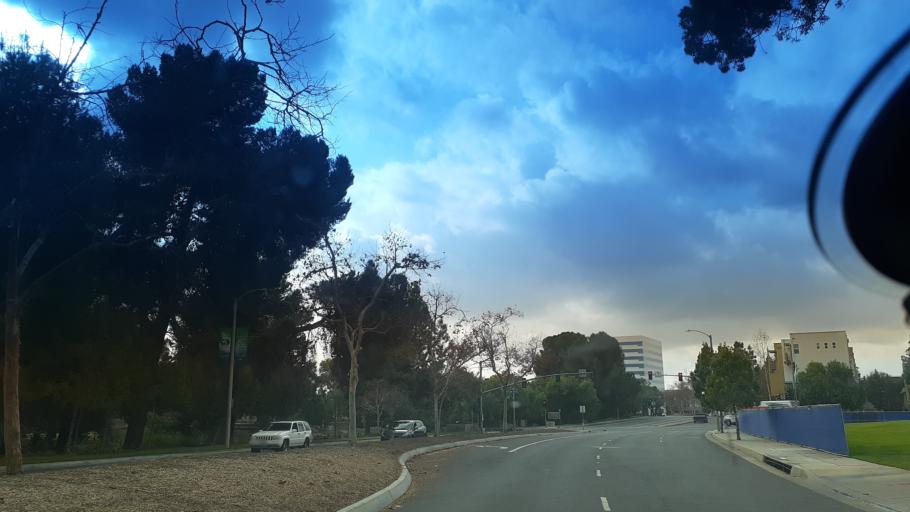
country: US
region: California
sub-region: Orange County
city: Orange
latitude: 33.7736
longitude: -117.8620
